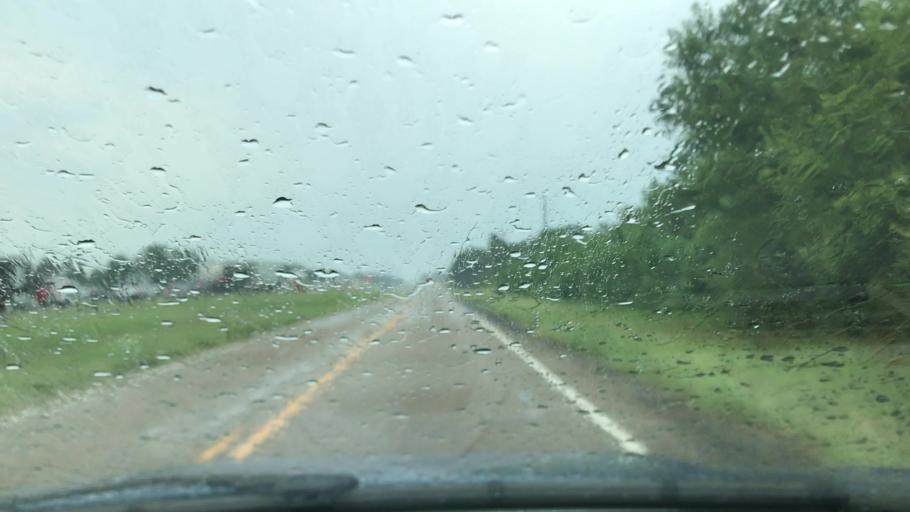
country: US
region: Texas
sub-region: Harrison County
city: Waskom
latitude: 32.4885
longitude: -94.1391
